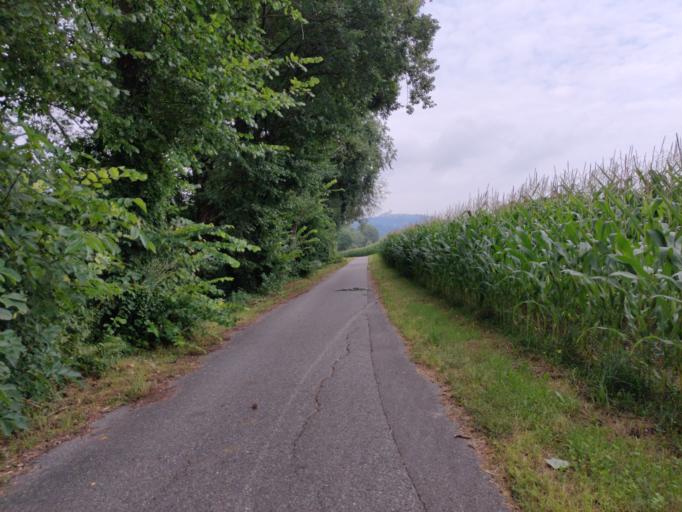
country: AT
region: Lower Austria
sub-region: Politischer Bezirk Melk
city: Marbach an der Donau
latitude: 48.2043
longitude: 15.1197
